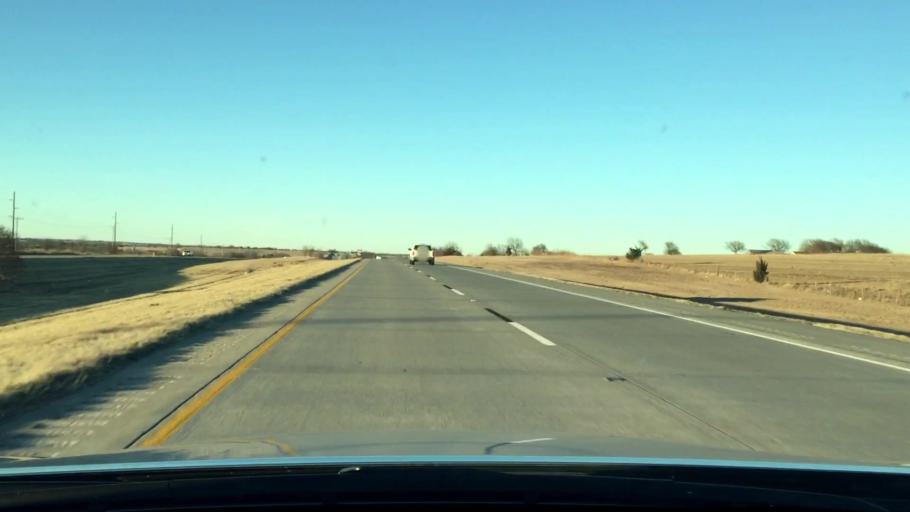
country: US
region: Oklahoma
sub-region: Love County
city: Marietta
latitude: 33.8653
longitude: -97.1339
